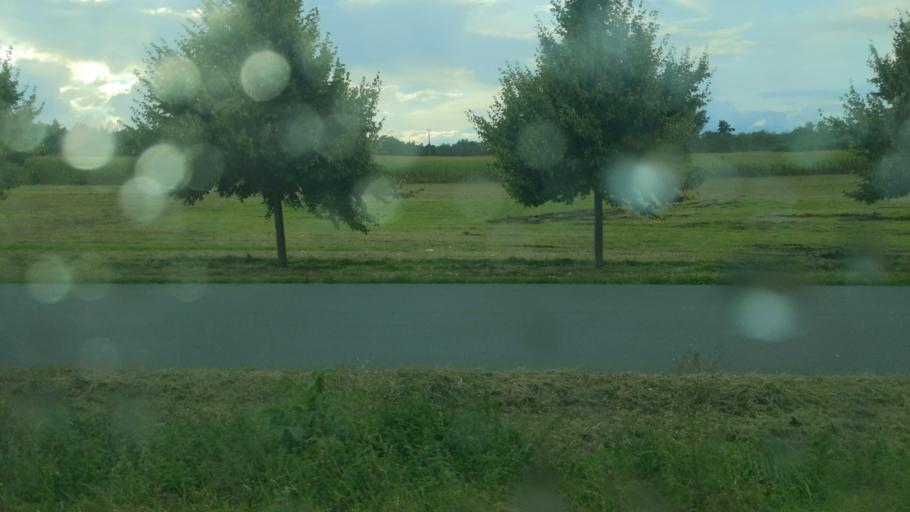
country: CZ
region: Central Bohemia
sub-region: Okres Nymburk
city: Sadska
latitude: 50.1284
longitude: 14.9636
